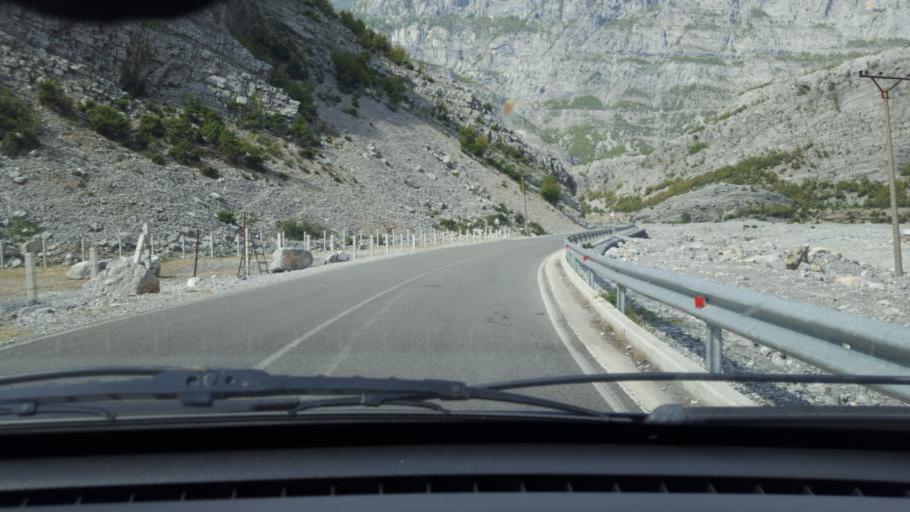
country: AL
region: Shkoder
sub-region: Rrethi i Malesia e Madhe
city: Kastrat
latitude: 42.4874
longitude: 19.5846
